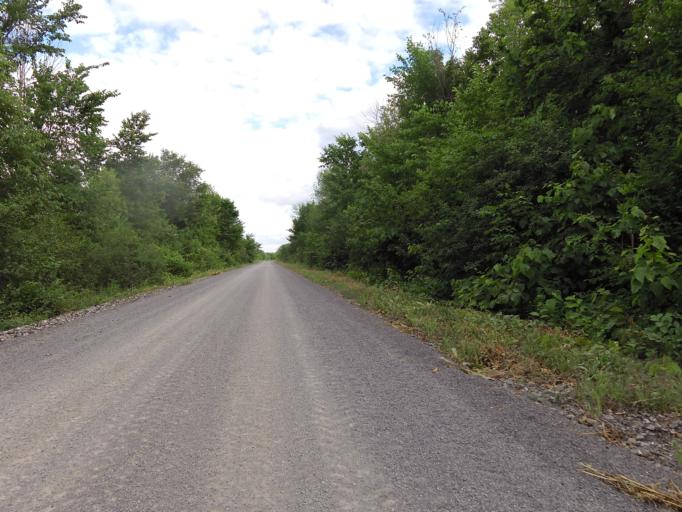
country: CA
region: Ontario
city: Arnprior
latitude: 45.2895
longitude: -76.2540
